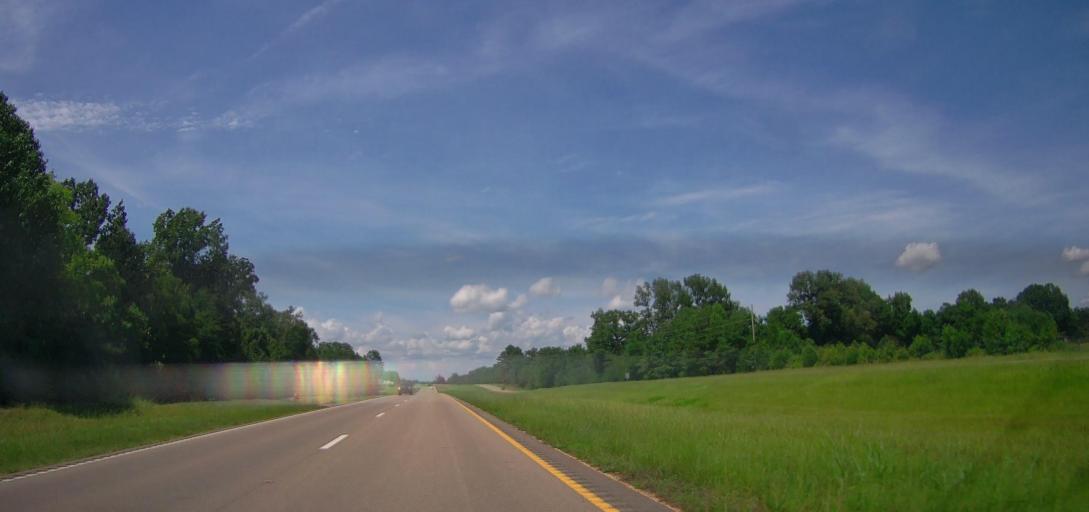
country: US
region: Mississippi
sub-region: Lee County
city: Nettleton
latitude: 33.9666
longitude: -88.6139
